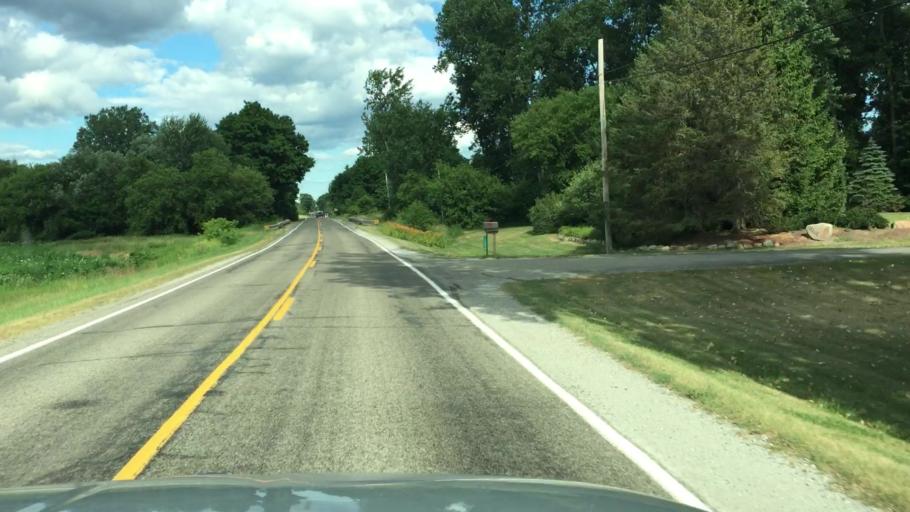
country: US
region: Michigan
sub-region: Saint Clair County
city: Yale
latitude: 43.1283
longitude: -82.8662
